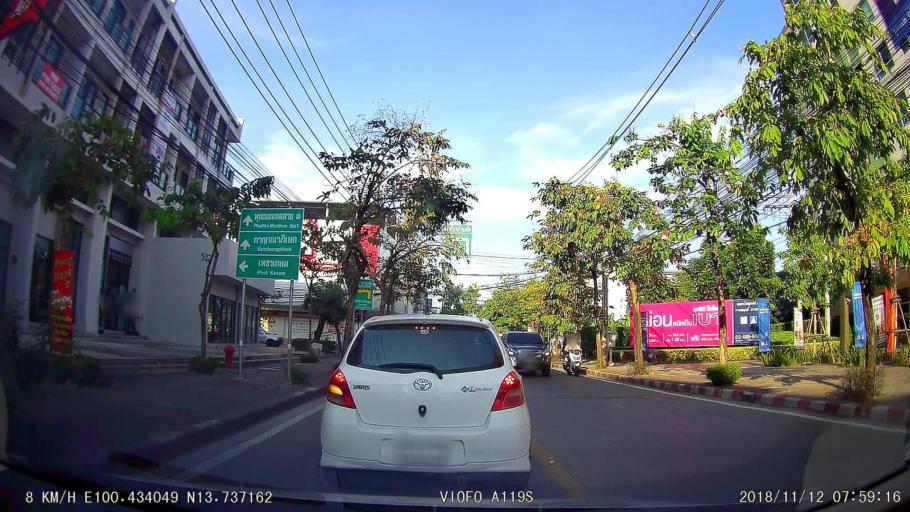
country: TH
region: Bangkok
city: Phasi Charoen
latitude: 13.7372
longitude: 100.4341
